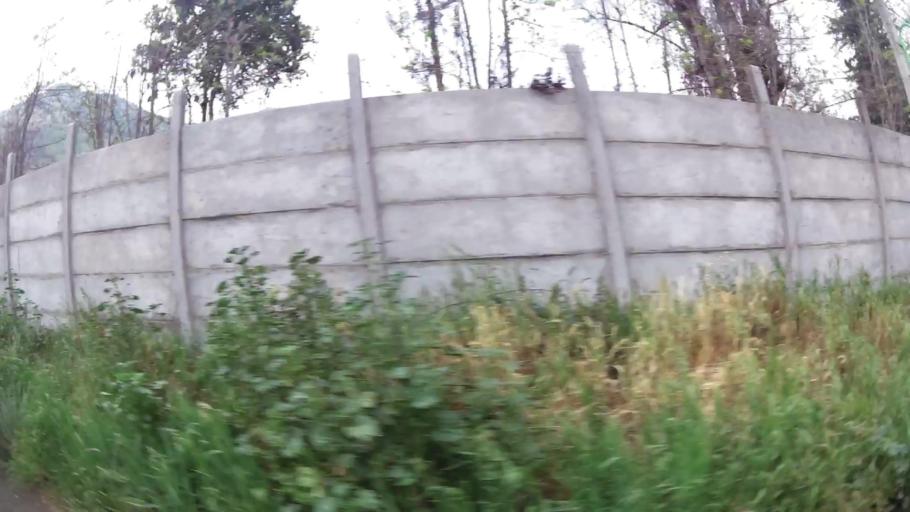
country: CL
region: Santiago Metropolitan
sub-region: Provincia de Chacabuco
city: Chicureo Abajo
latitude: -33.2424
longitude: -70.6745
